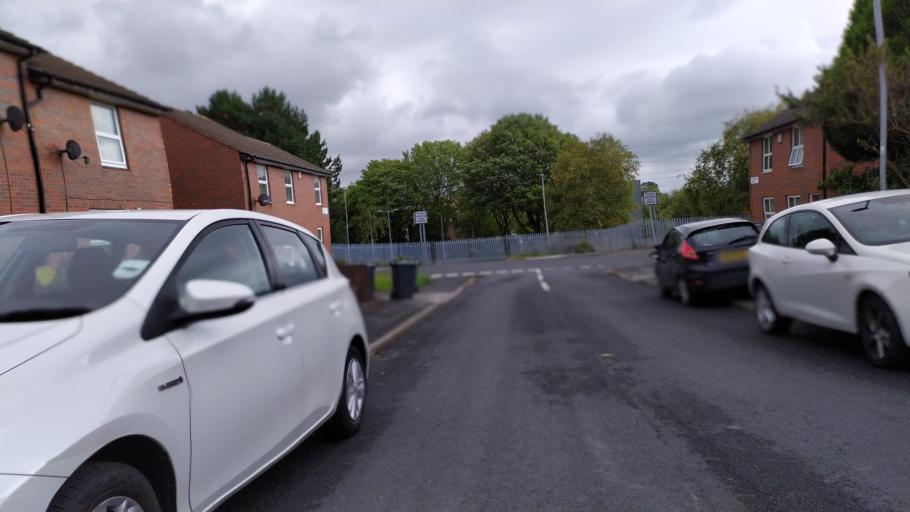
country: GB
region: England
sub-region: City and Borough of Leeds
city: Leeds
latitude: 53.8138
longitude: -1.5487
